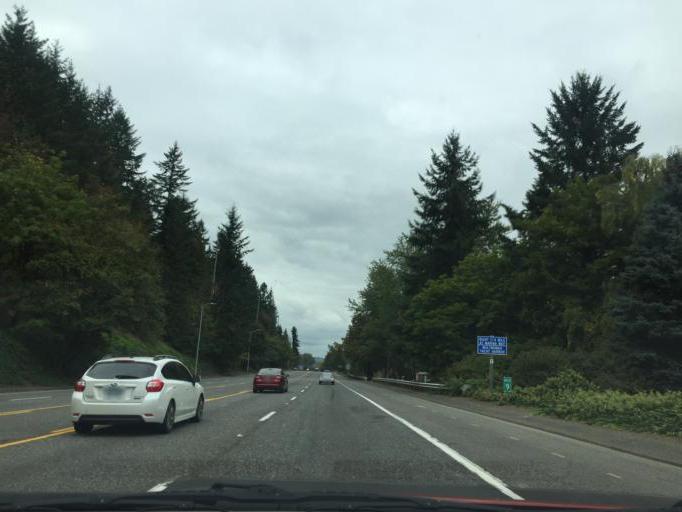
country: US
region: Oregon
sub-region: Washington County
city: Oak Hills
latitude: 45.6073
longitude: -122.7925
